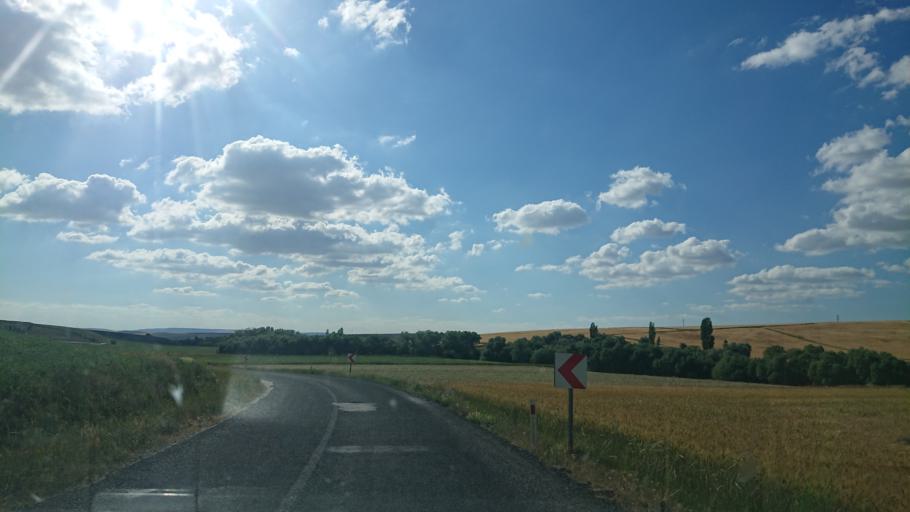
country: TR
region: Aksaray
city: Ortakoy
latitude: 38.7560
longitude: 33.9217
